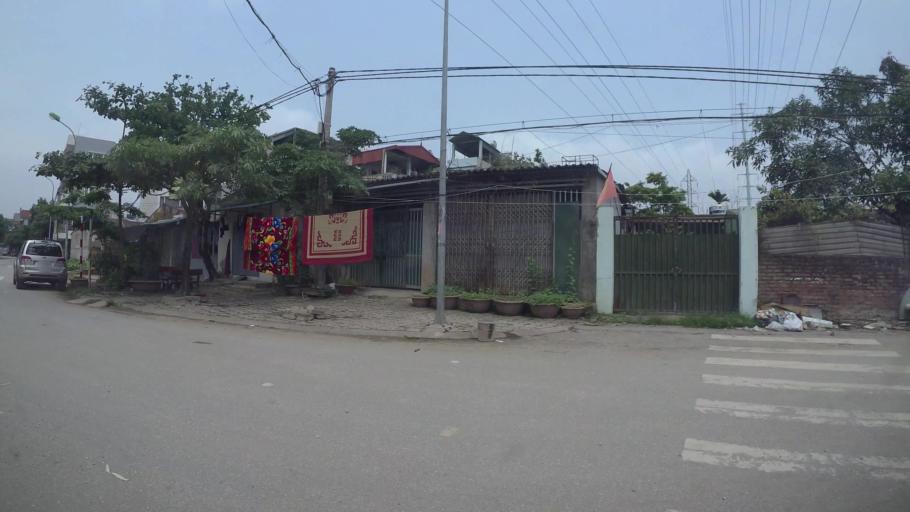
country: VN
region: Ha Noi
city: Tay Ho
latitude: 21.0861
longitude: 105.7957
